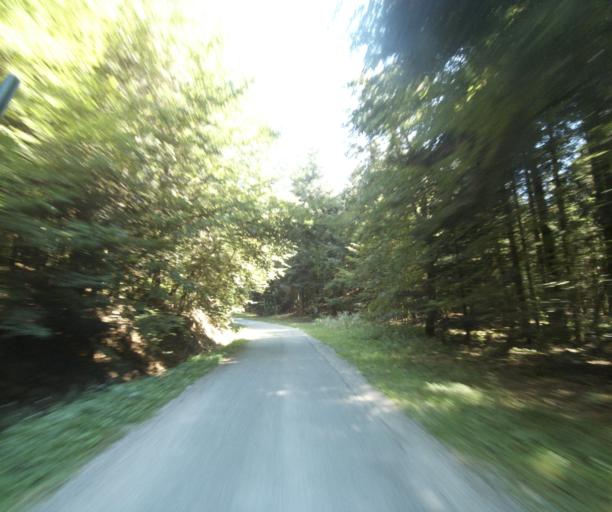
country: FR
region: Lorraine
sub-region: Departement des Vosges
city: Epinal
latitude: 48.1680
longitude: 6.4766
